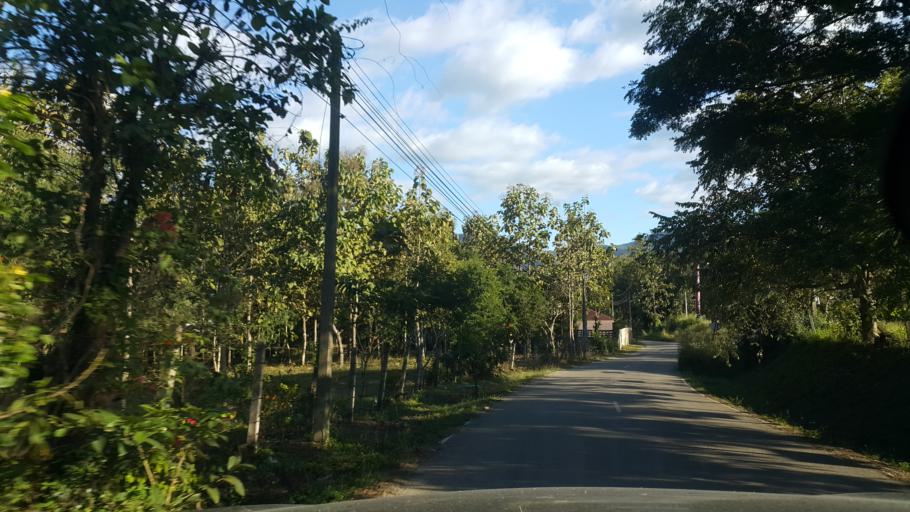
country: TH
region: Chiang Mai
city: Mae On
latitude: 18.7726
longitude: 99.2502
